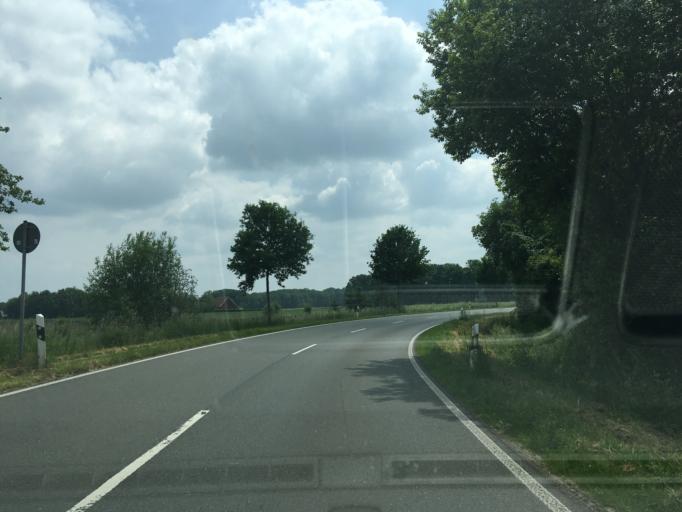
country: DE
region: North Rhine-Westphalia
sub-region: Regierungsbezirk Munster
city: Sudlohn
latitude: 51.9017
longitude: 6.8642
